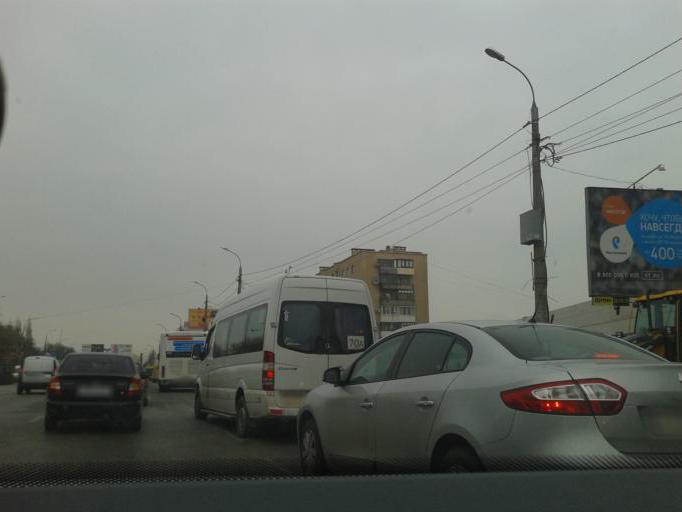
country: RU
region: Volgograd
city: Volgograd
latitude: 48.6732
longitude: 44.4433
